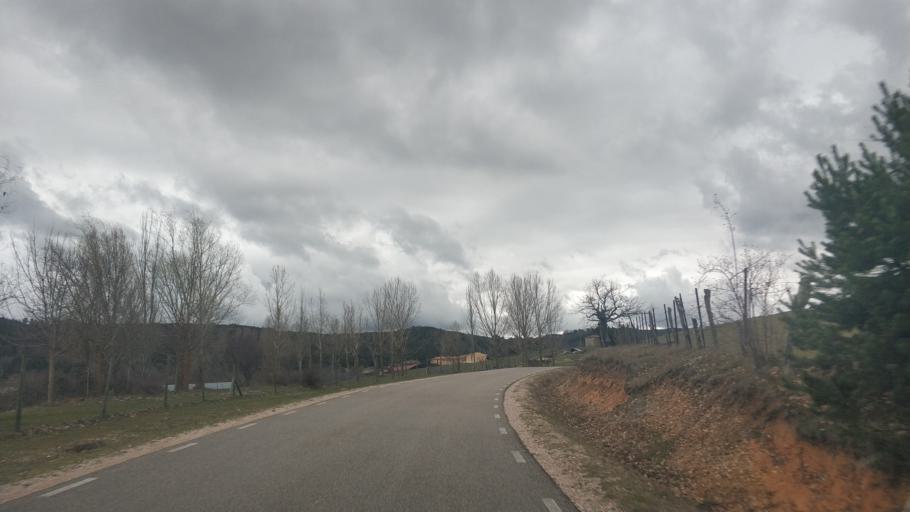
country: ES
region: Castille and Leon
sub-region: Provincia de Burgos
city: Canicosa de la Sierra
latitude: 41.9417
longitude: -3.0366
